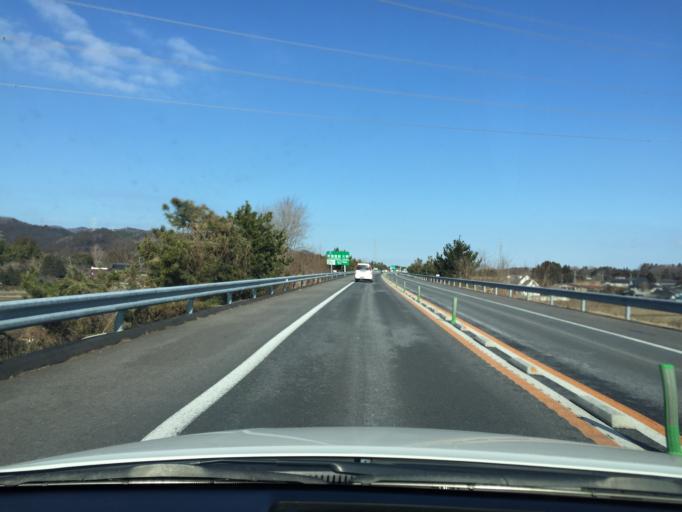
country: JP
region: Fukushima
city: Namie
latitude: 37.3643
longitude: 140.9690
